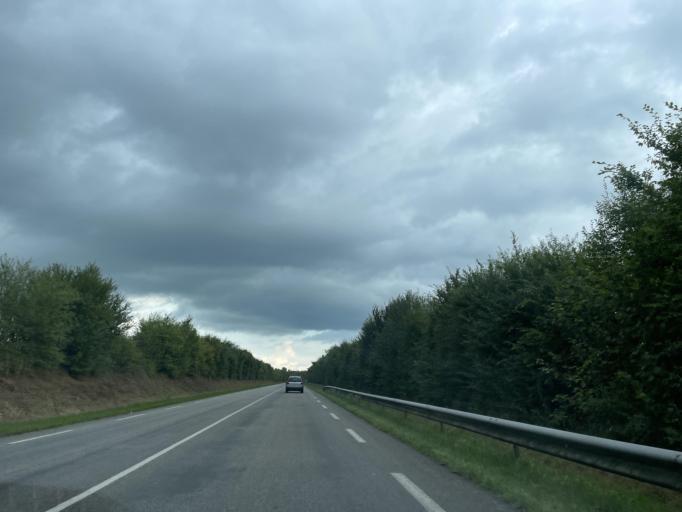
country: FR
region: Haute-Normandie
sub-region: Departement de la Seine-Maritime
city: Forges-les-Eaux
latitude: 49.6000
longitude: 1.5393
